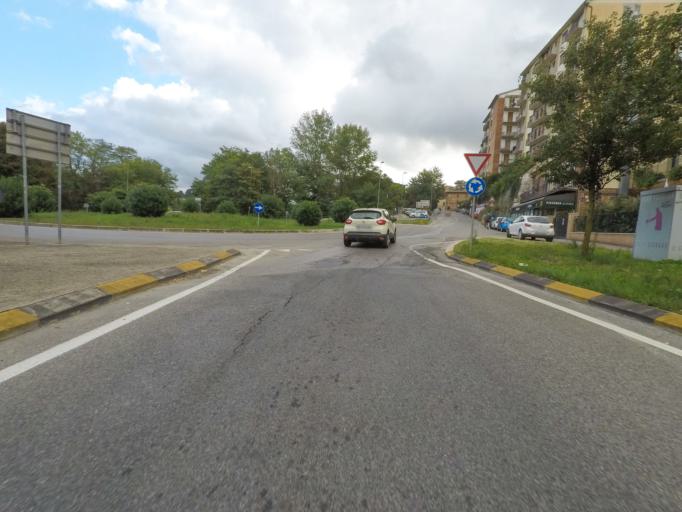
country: IT
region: Tuscany
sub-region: Provincia di Siena
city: Siena
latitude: 43.3274
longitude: 11.3317
